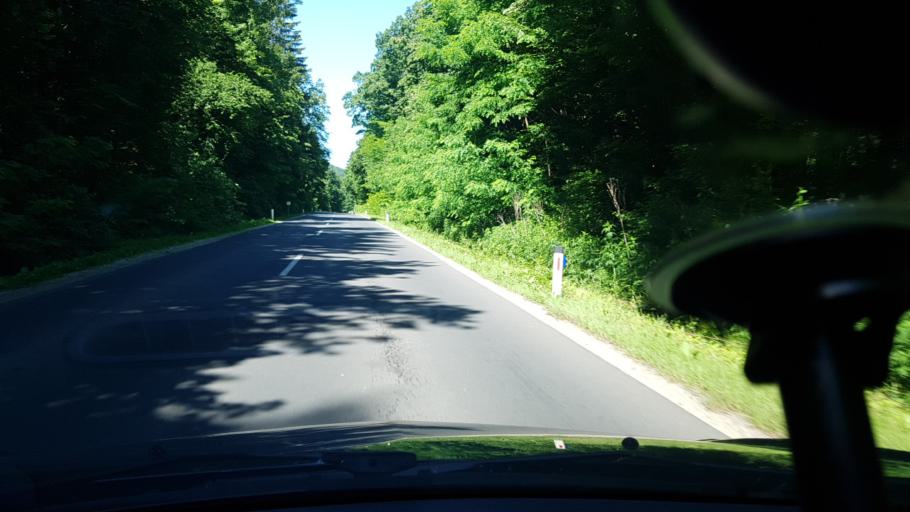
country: SI
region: Slovenska Bistrica
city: Slovenska Bistrica
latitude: 46.3824
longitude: 15.5187
